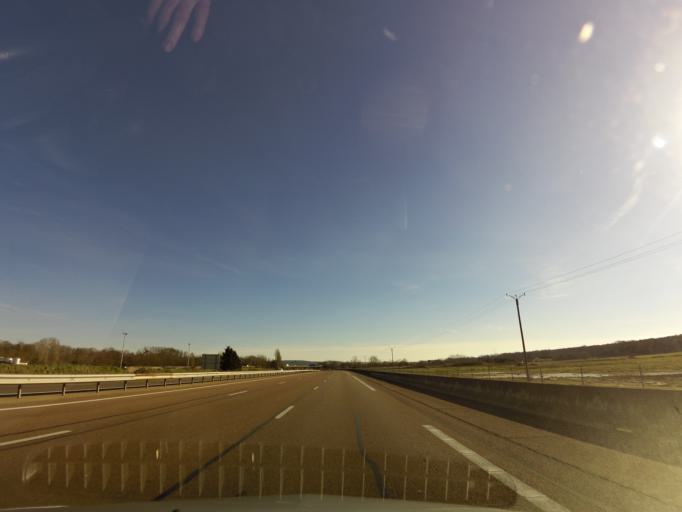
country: FR
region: Bourgogne
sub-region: Departement de l'Yonne
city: Appoigny
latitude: 47.8595
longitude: 3.5374
